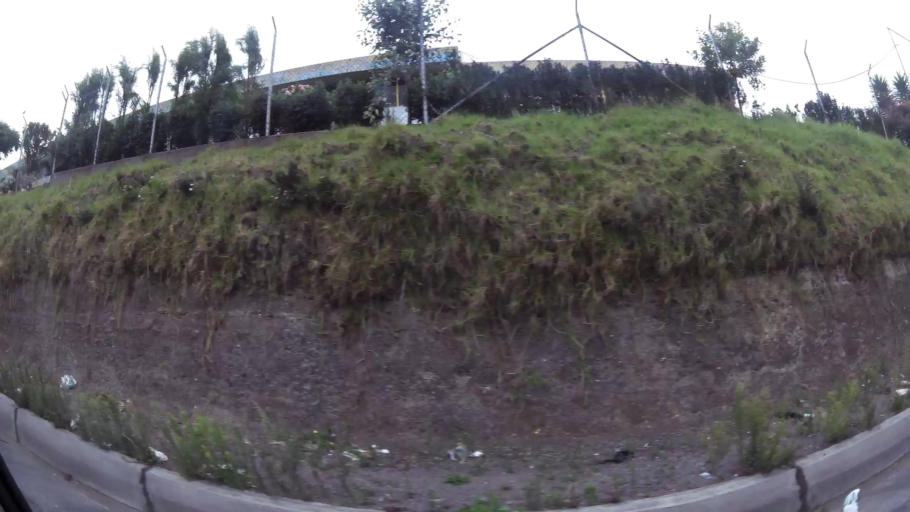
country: EC
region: Cotopaxi
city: Latacunga
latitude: -0.9428
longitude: -78.6154
